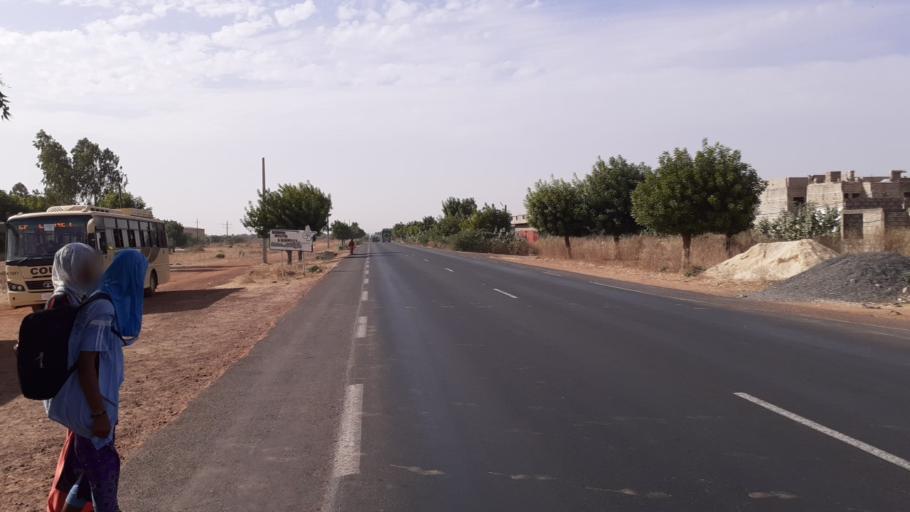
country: SN
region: Kaolack
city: Kaolack
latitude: 14.1641
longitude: -16.1237
